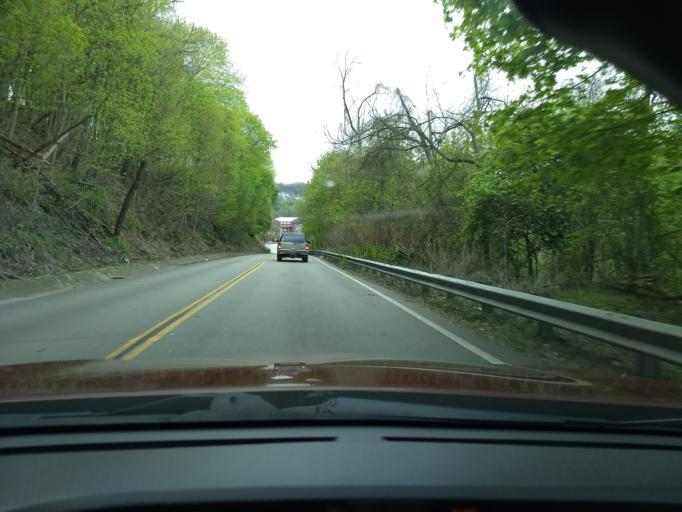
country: US
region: Pennsylvania
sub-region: Allegheny County
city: Wilmerding
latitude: 40.3925
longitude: -79.8021
